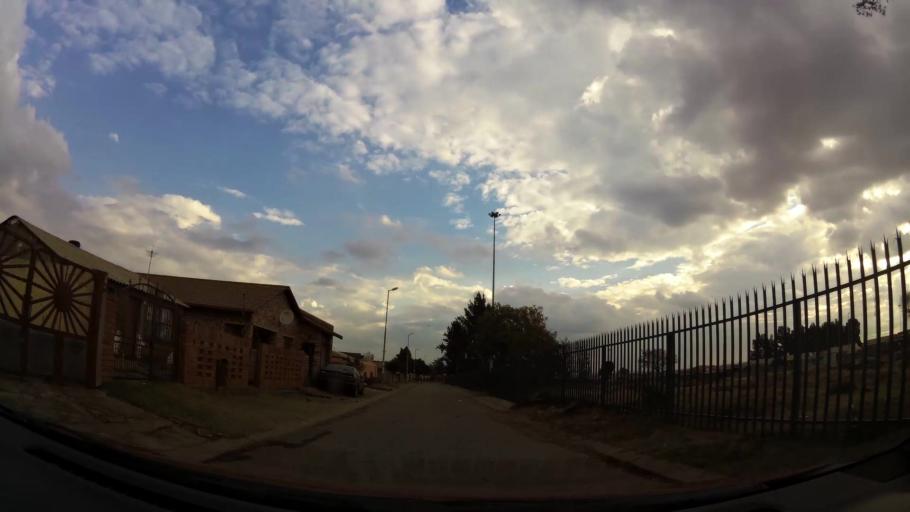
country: ZA
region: Gauteng
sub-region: City of Johannesburg Metropolitan Municipality
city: Soweto
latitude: -26.2403
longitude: 27.8266
